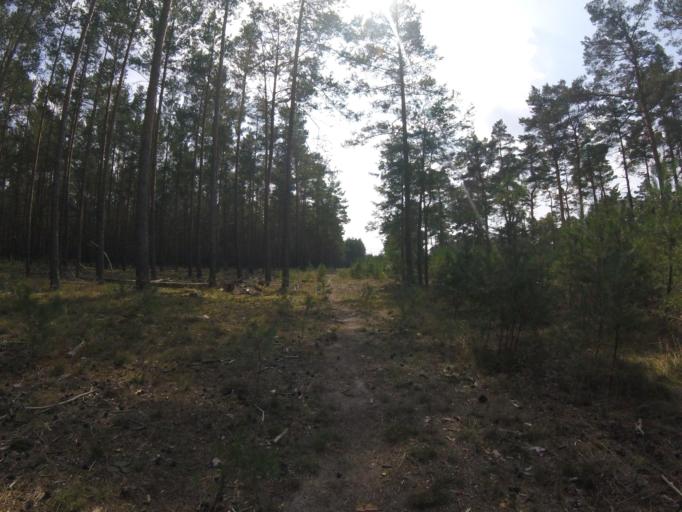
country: DE
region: Brandenburg
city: Bestensee
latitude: 52.2748
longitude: 13.6652
